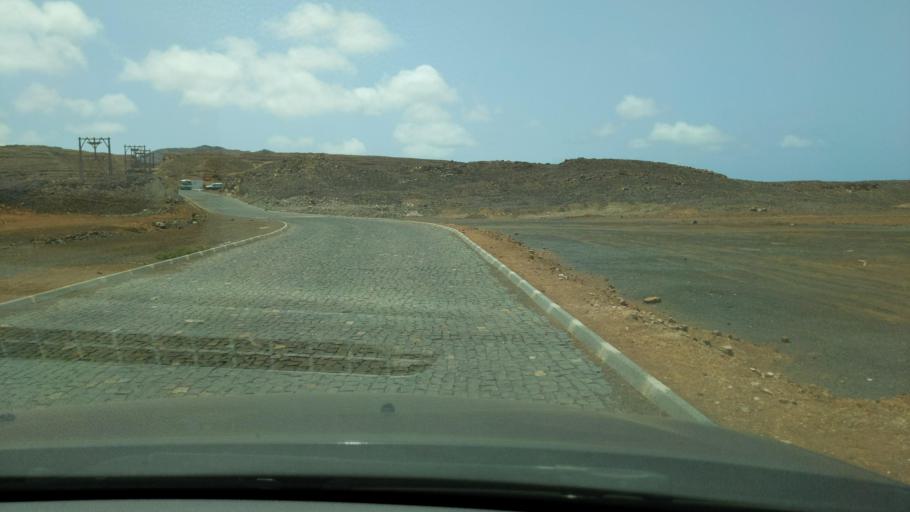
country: CV
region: Sal
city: Espargos
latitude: 16.7671
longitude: -22.8948
